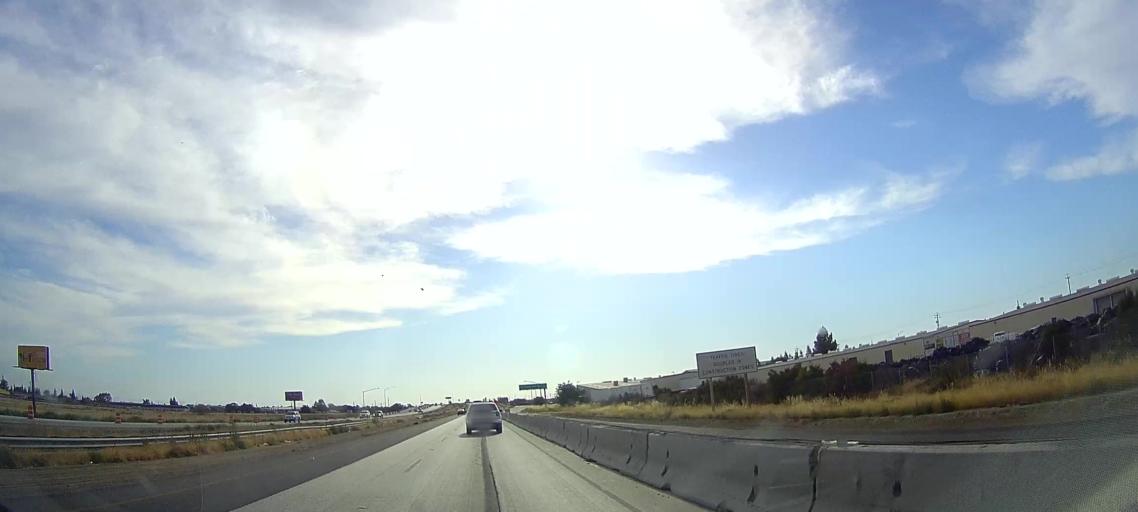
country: US
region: California
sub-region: Kern County
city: Bakersfield
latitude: 35.3529
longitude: -118.9593
